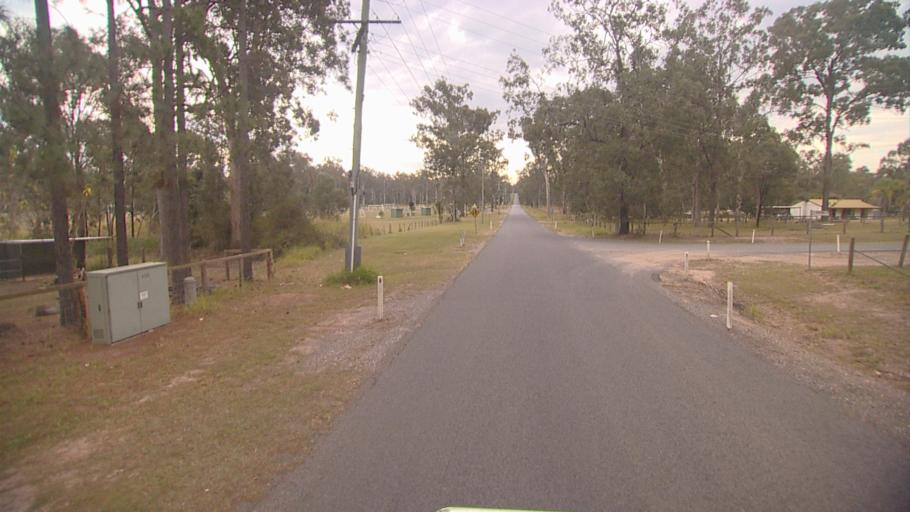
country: AU
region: Queensland
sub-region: Logan
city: Chambers Flat
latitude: -27.7918
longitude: 153.1211
